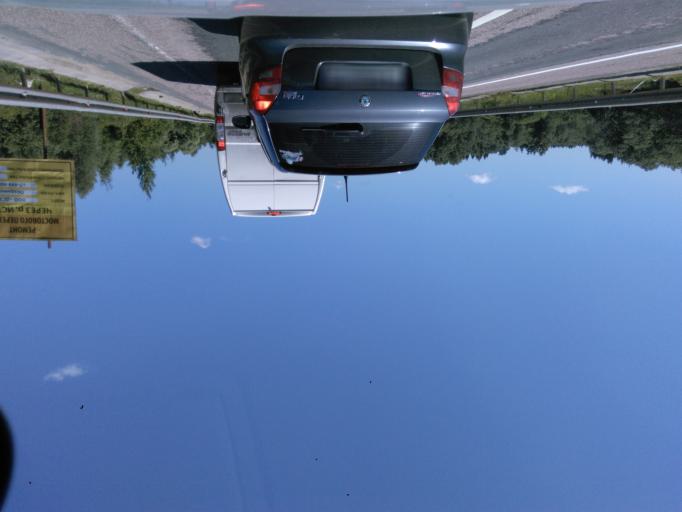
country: RU
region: Moskovskaya
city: Solnechnogorsk
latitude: 56.1435
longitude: 36.9525
